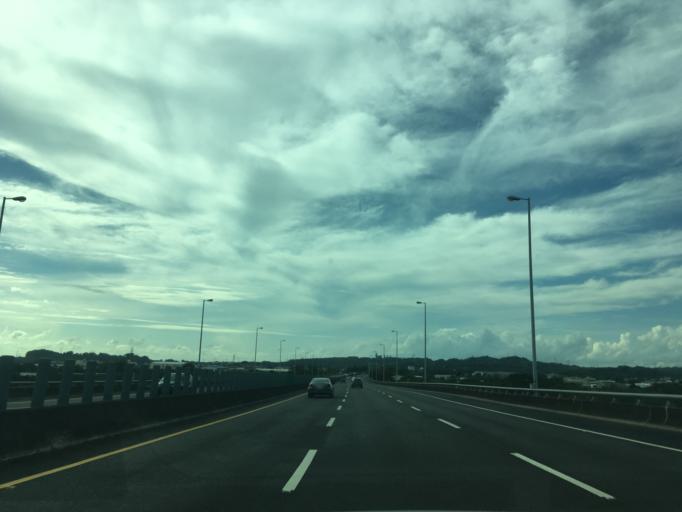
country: TW
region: Taiwan
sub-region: Chiayi
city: Jiayi Shi
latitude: 23.5040
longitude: 120.4910
